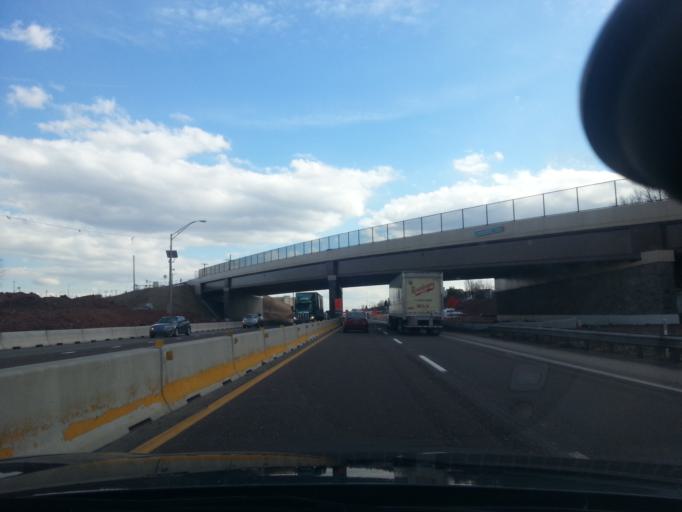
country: US
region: Pennsylvania
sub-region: Montgomery County
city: Kulpsville
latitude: 40.2491
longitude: -75.3462
